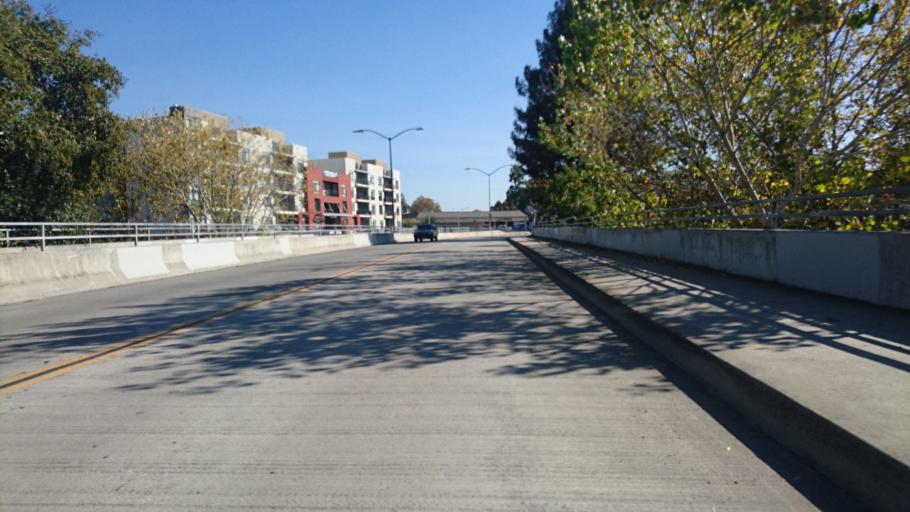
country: US
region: California
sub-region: Santa Clara County
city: Campbell
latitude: 37.2922
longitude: -121.9344
